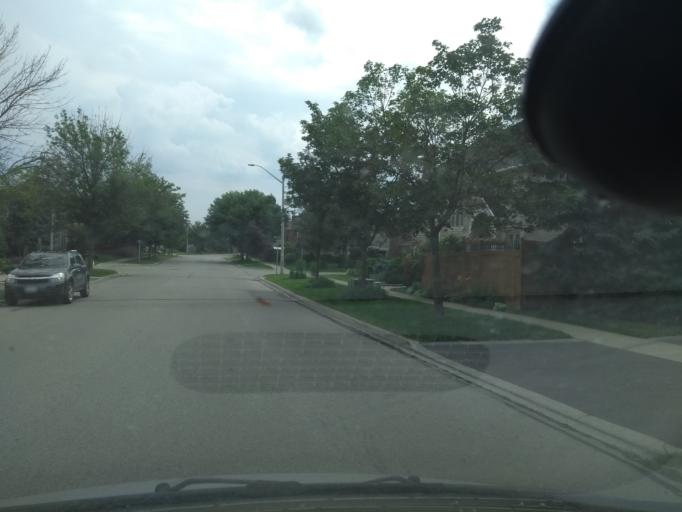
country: CA
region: Ontario
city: Mississauga
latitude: 43.6224
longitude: -79.6536
